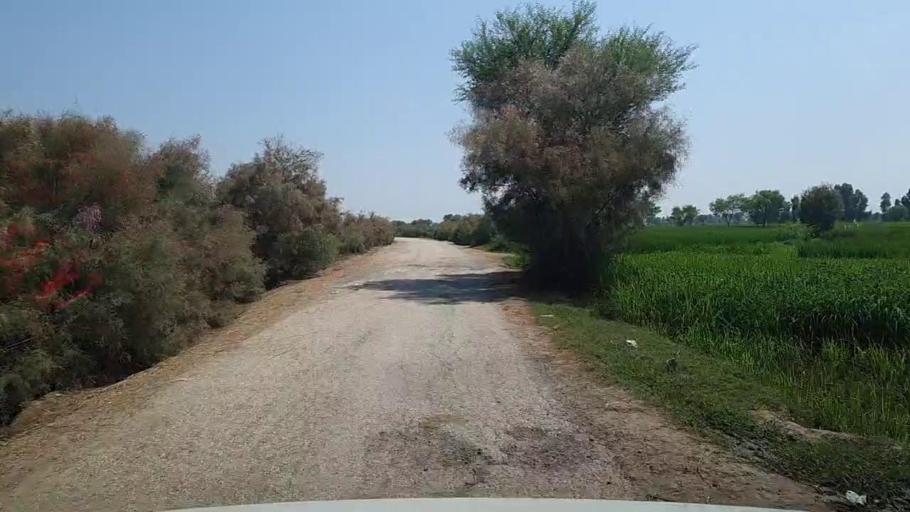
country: PK
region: Sindh
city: Kandhkot
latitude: 28.2798
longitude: 69.3548
